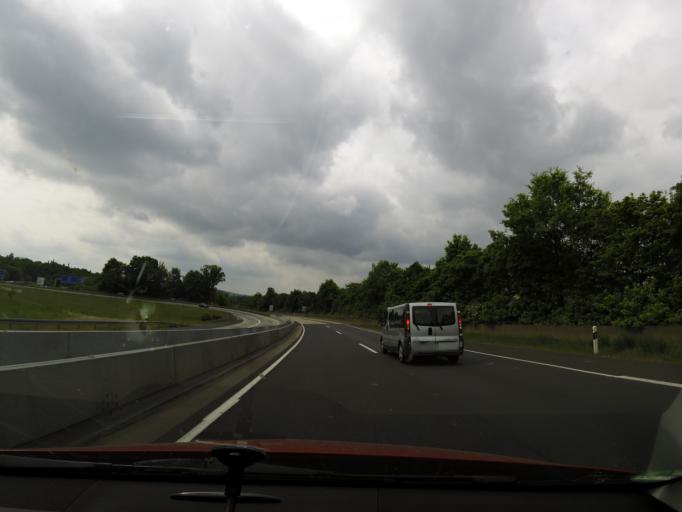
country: DE
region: Hesse
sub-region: Regierungsbezirk Kassel
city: Kirchheim
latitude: 50.8372
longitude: 9.5784
